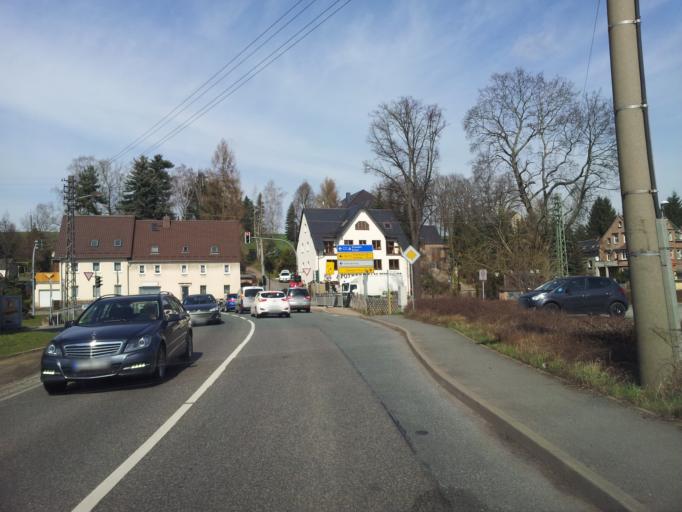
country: DE
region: Saxony
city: Oberlungwitz
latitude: 50.7816
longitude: 12.7013
